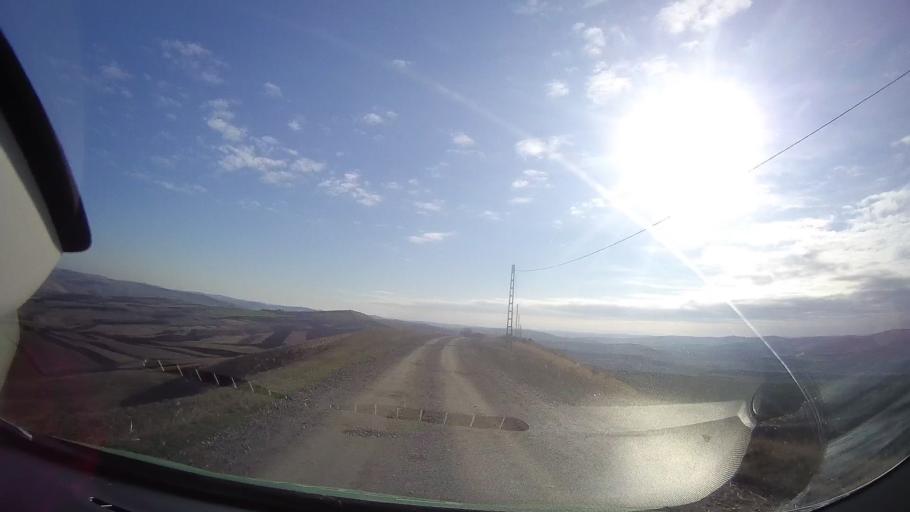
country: RO
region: Mures
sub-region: Comuna Saulia
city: Saulia
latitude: 46.5900
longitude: 24.2211
